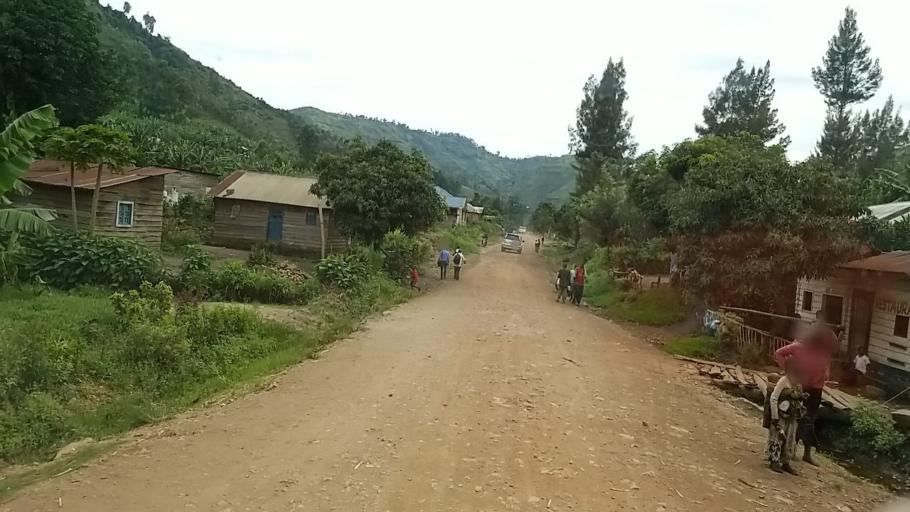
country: CD
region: Nord Kivu
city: Sake
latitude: -1.7266
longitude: 29.0101
